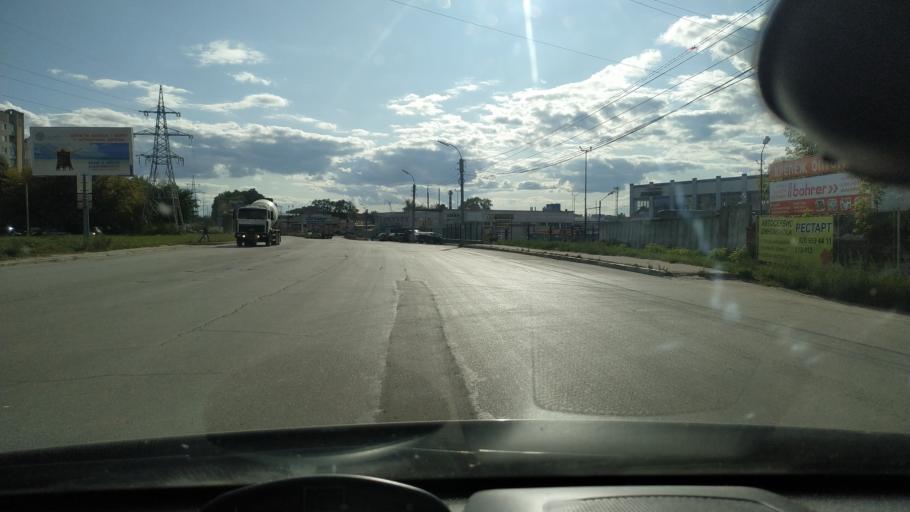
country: RU
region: Rjazan
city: Ryazan'
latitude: 54.6181
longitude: 39.6950
